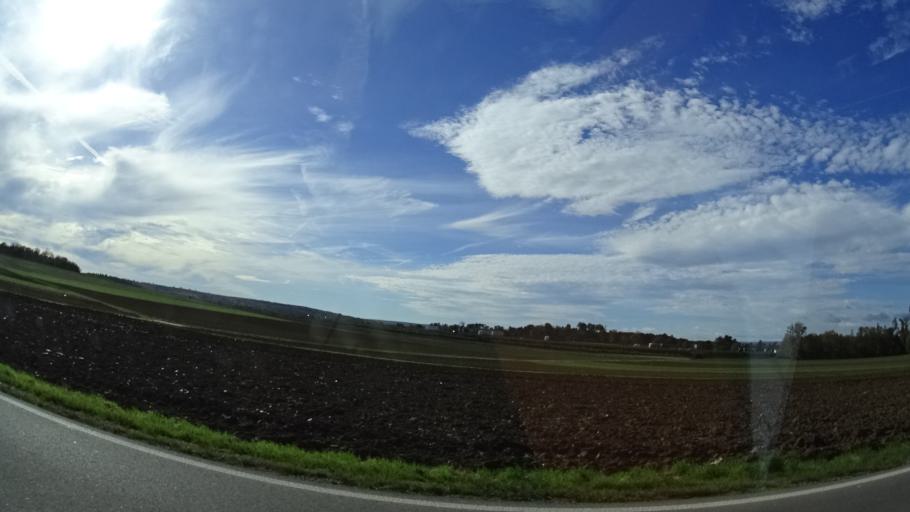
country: DE
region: Baden-Wuerttemberg
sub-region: Karlsruhe Region
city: Heimsheim
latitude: 48.8284
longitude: 8.8851
